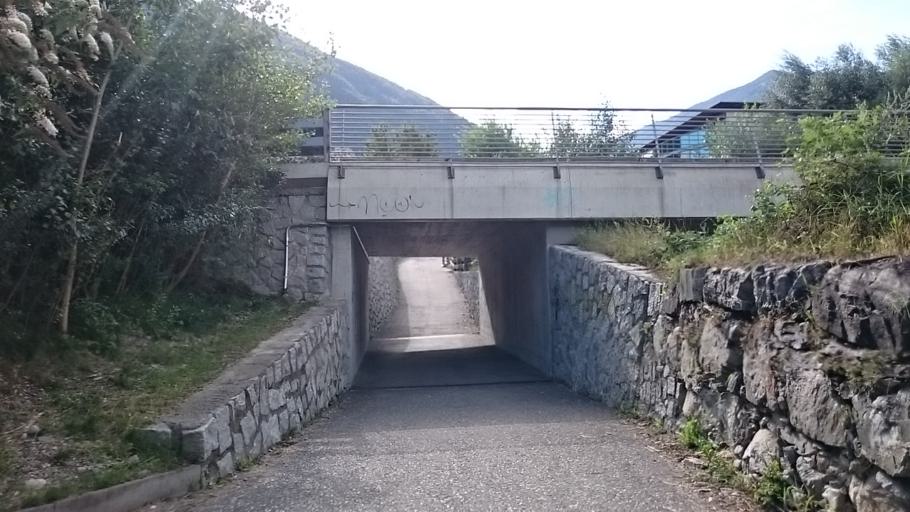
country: IT
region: Trentino-Alto Adige
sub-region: Bolzano
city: Leone-Santa Elisabetta
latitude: 46.7351
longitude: 11.6482
